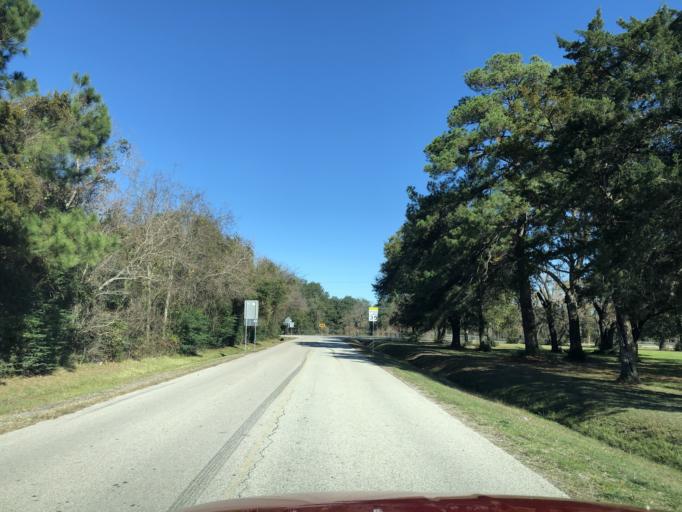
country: US
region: Texas
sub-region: Harris County
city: Oak Cliff Place
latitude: 29.9443
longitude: -95.6547
